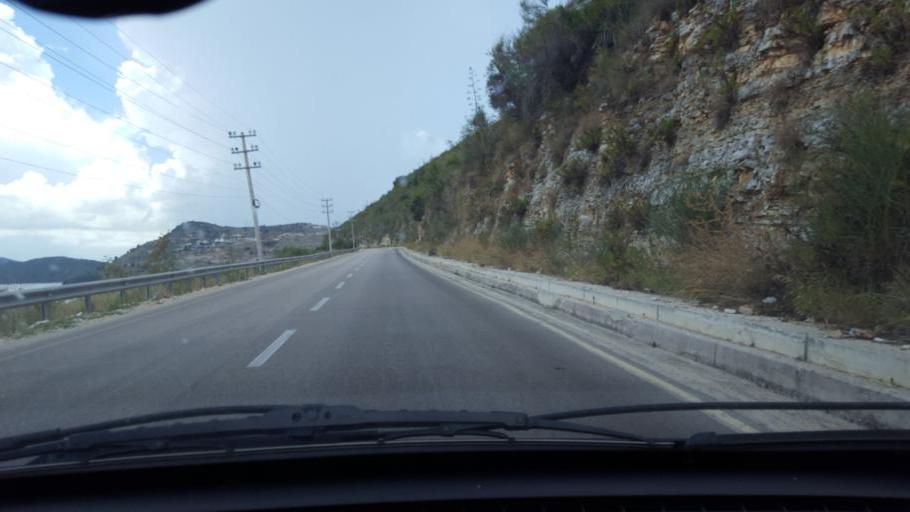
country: AL
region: Vlore
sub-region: Rrethi i Sarandes
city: Sarande
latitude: 39.8177
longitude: 20.0164
